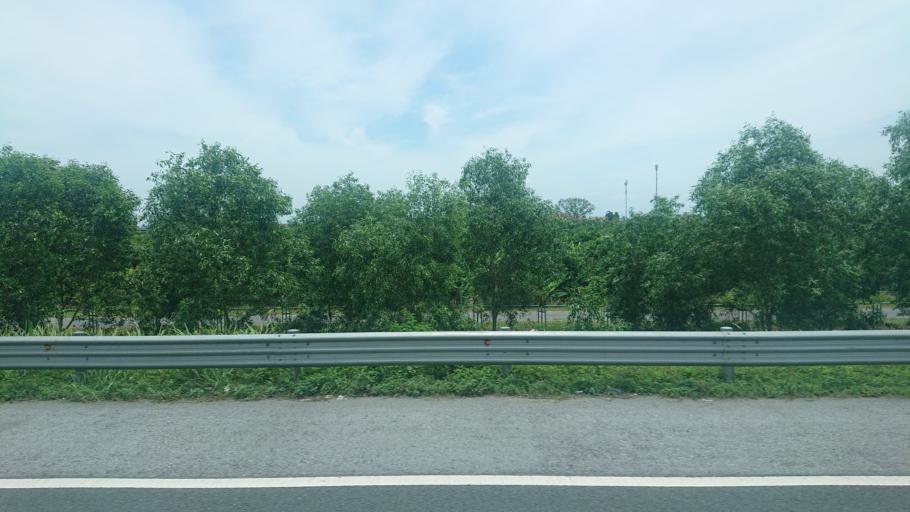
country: VN
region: Hai Duong
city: Tu Ky
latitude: 20.8286
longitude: 106.4547
